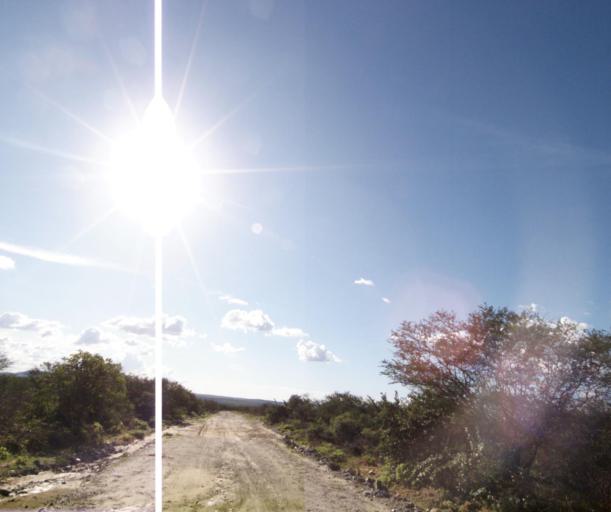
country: BR
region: Bahia
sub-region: Tanhacu
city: Tanhacu
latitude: -14.1876
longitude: -40.9827
